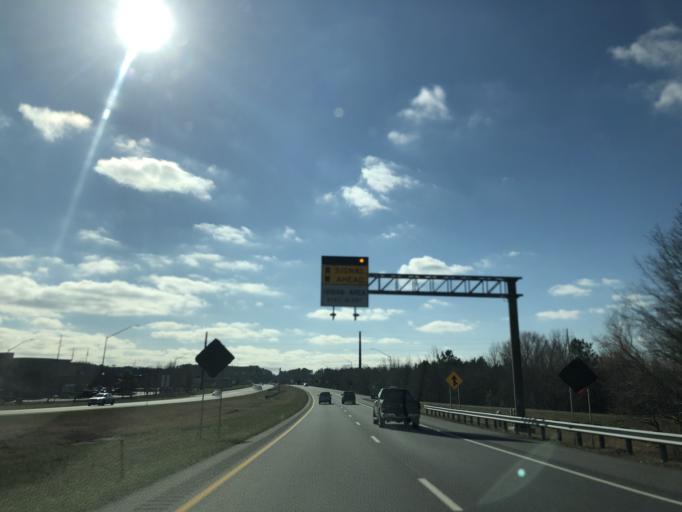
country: US
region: Maryland
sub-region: Worcester County
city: Berlin
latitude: 38.3409
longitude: -75.2133
